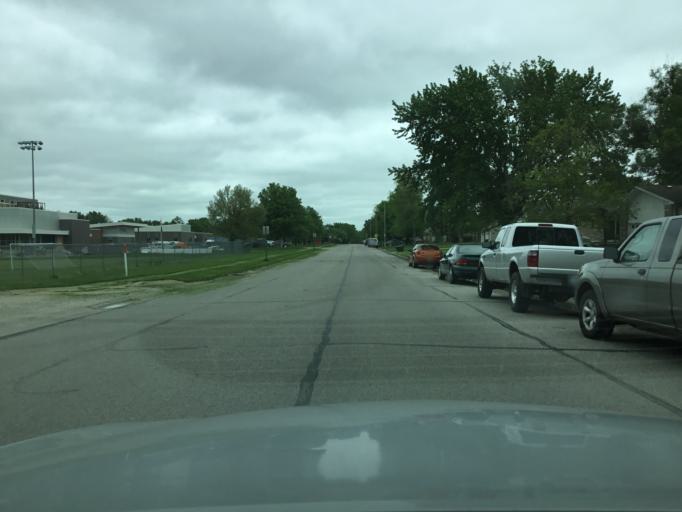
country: US
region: Kansas
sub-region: Franklin County
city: Ottawa
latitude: 38.5985
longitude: -95.2770
